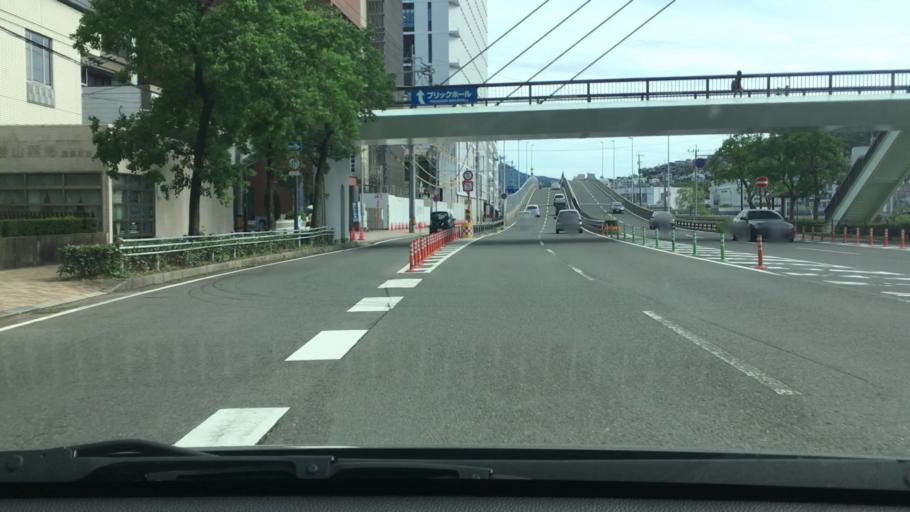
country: JP
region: Nagasaki
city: Nagasaki-shi
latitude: 32.7662
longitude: 129.8623
